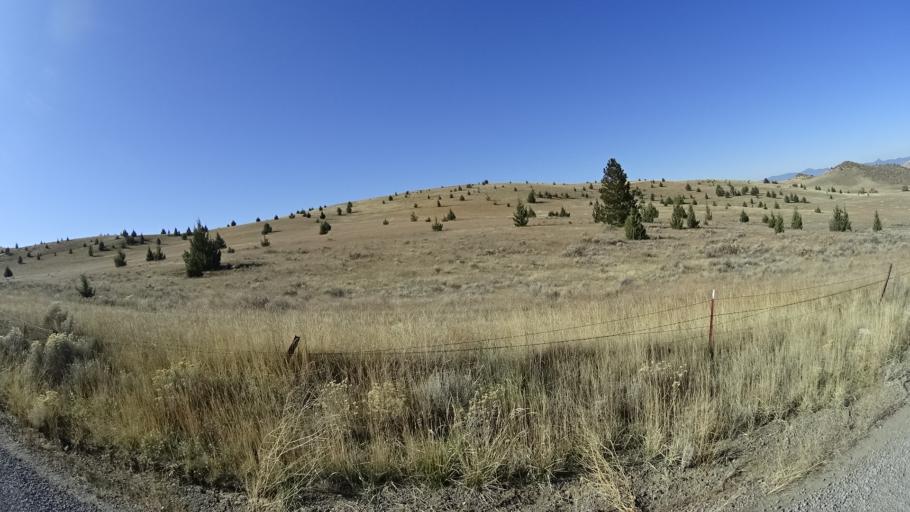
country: US
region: California
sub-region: Siskiyou County
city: Montague
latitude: 41.7778
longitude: -122.3591
